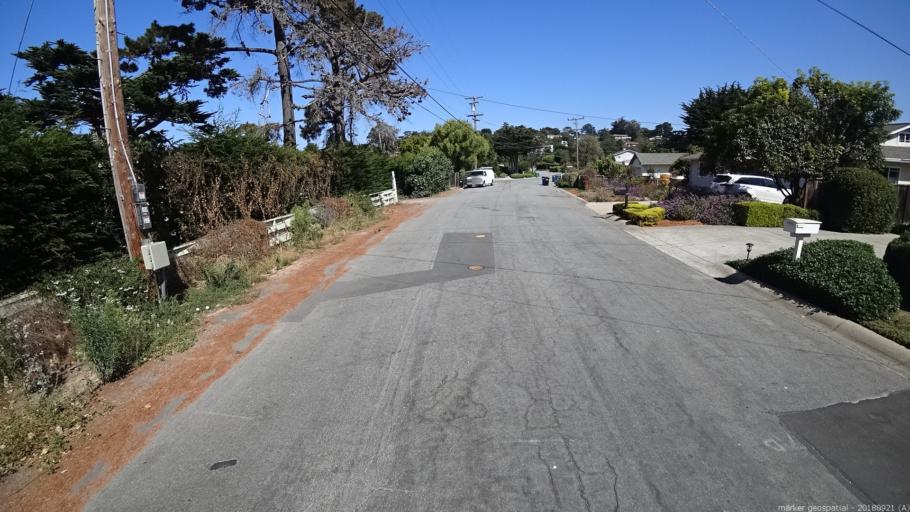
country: US
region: California
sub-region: Monterey County
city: Carmel-by-the-Sea
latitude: 36.5383
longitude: -121.9133
